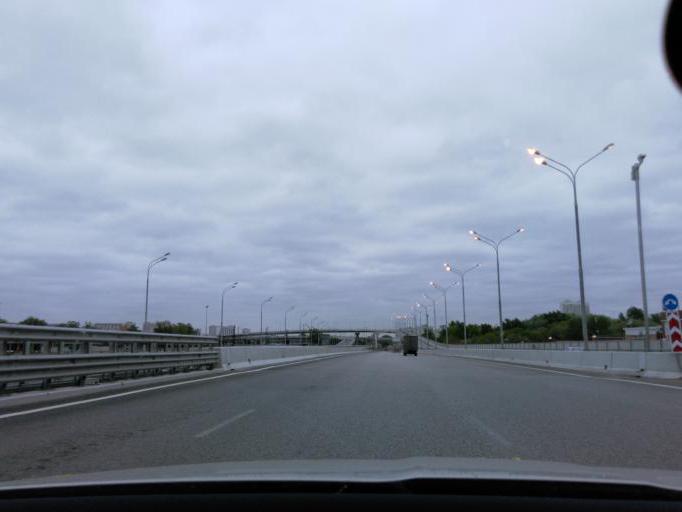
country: RU
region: Moscow
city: Businovo
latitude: 55.8760
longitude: 37.4933
